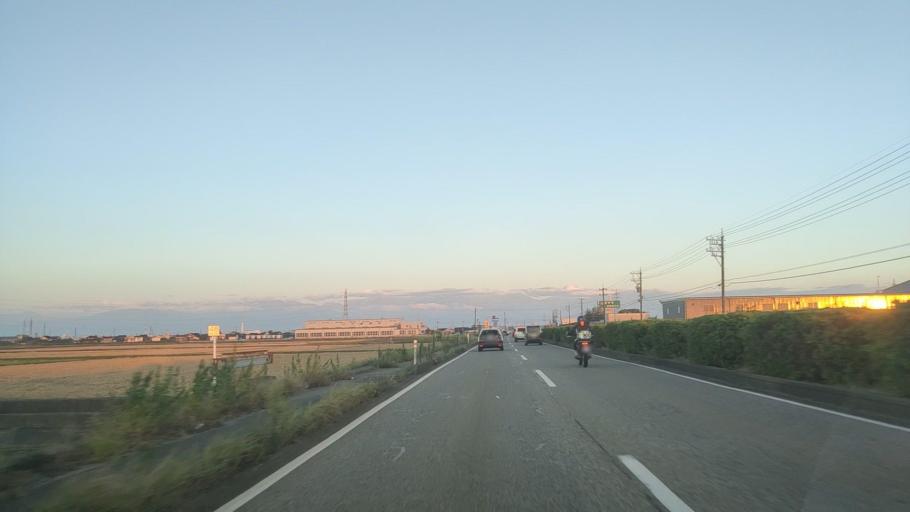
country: JP
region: Toyama
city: Nishishinminato
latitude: 36.7474
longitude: 137.0969
